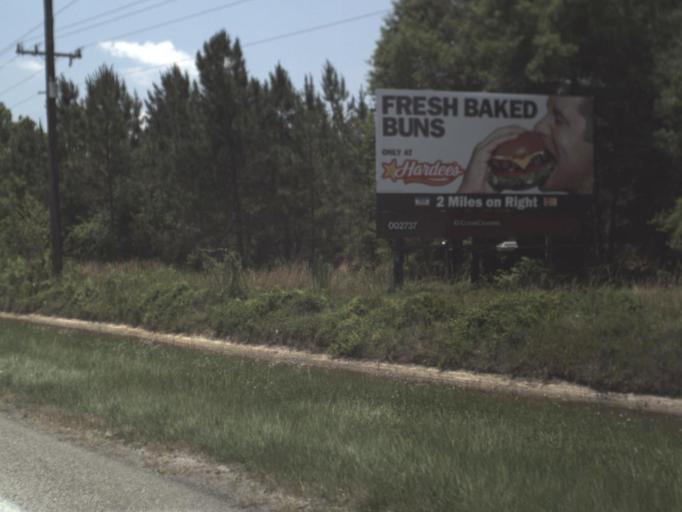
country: US
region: Florida
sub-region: Bradford County
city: Starke
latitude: 29.9747
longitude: -82.1008
